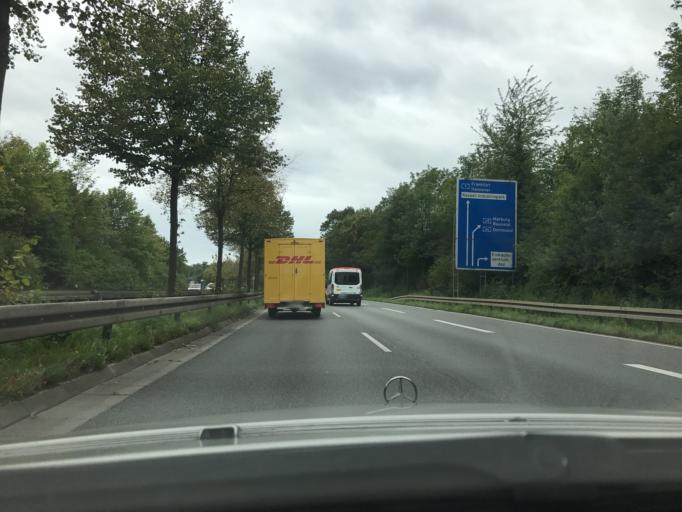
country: DE
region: Hesse
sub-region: Regierungsbezirk Kassel
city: Fuldabruck
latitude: 51.2914
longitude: 9.4802
